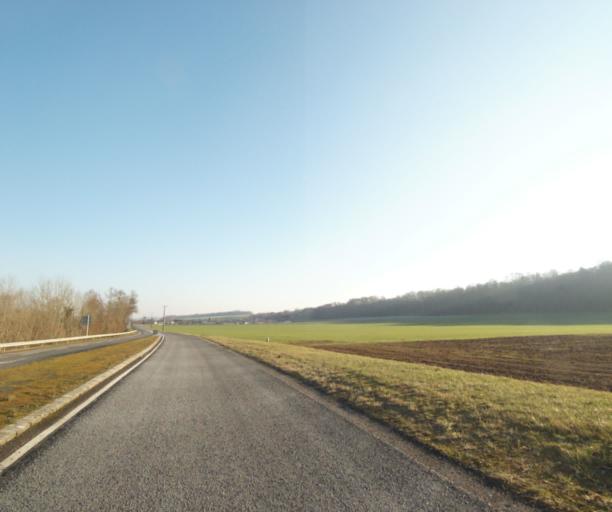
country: FR
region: Champagne-Ardenne
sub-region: Departement de la Haute-Marne
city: Bienville
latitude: 48.5671
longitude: 5.0416
